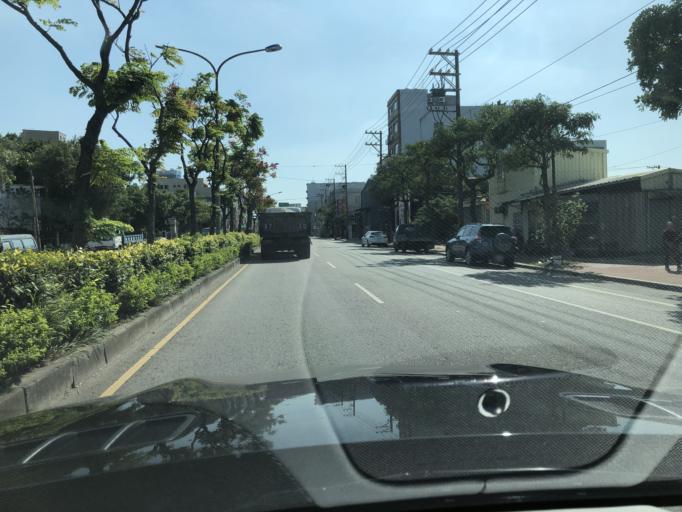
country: TW
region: Taiwan
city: Taoyuan City
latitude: 25.0747
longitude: 121.2852
